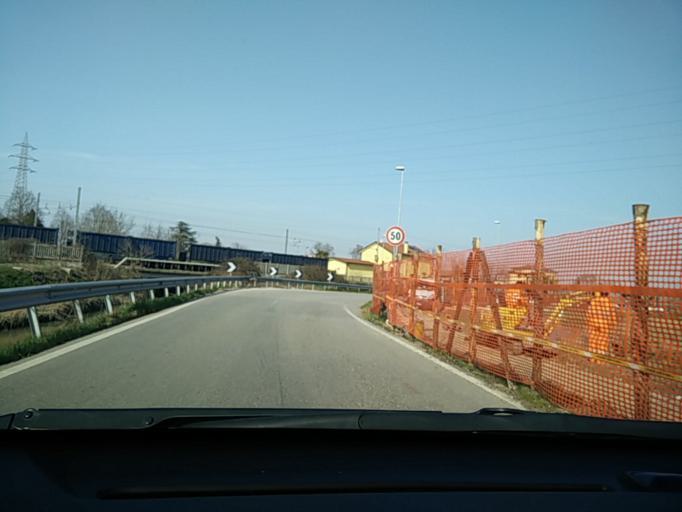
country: IT
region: Veneto
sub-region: Provincia di Venezia
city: Fossalta di Piave
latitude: 45.6232
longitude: 12.4984
